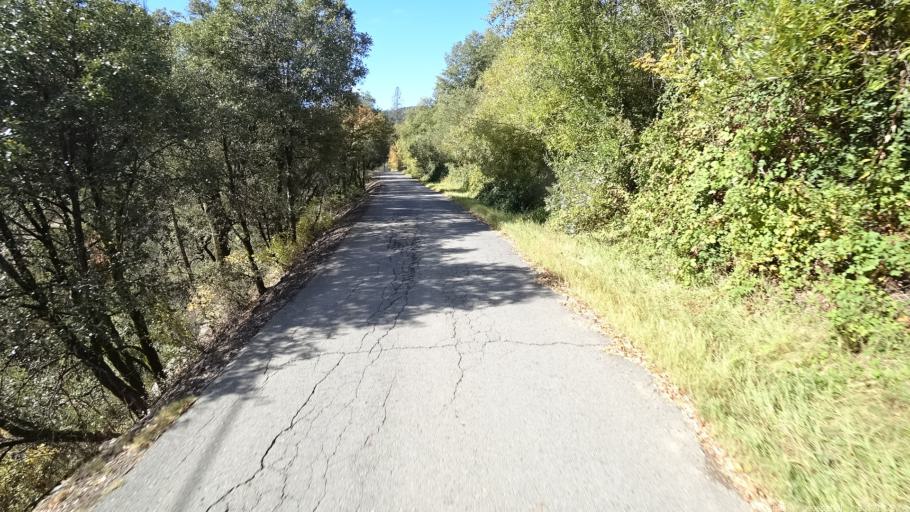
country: US
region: California
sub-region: Siskiyou County
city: Dunsmuir
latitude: 40.9753
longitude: -122.4354
